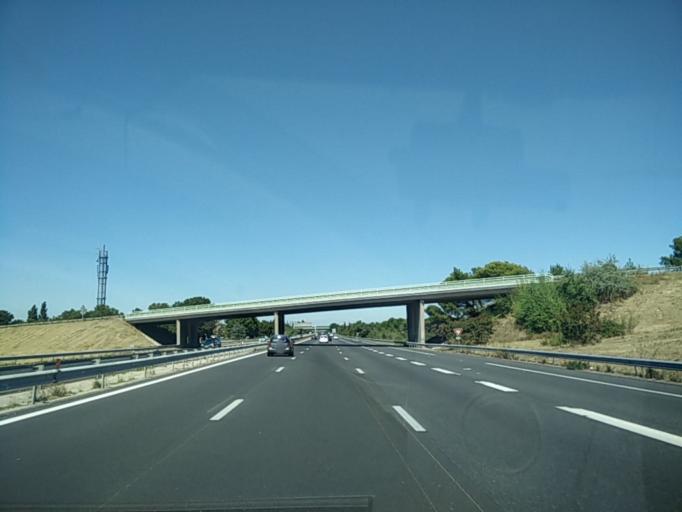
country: FR
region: Provence-Alpes-Cote d'Azur
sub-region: Departement du Vaucluse
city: Vedene
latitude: 43.9799
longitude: 4.8932
